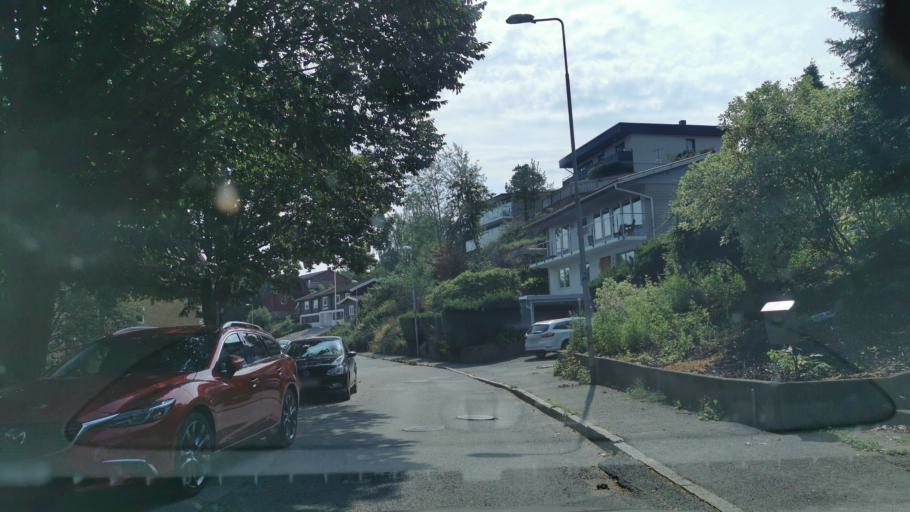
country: SE
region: Vaestra Goetaland
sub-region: Molndal
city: Moelndal
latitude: 57.6755
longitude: 11.9911
